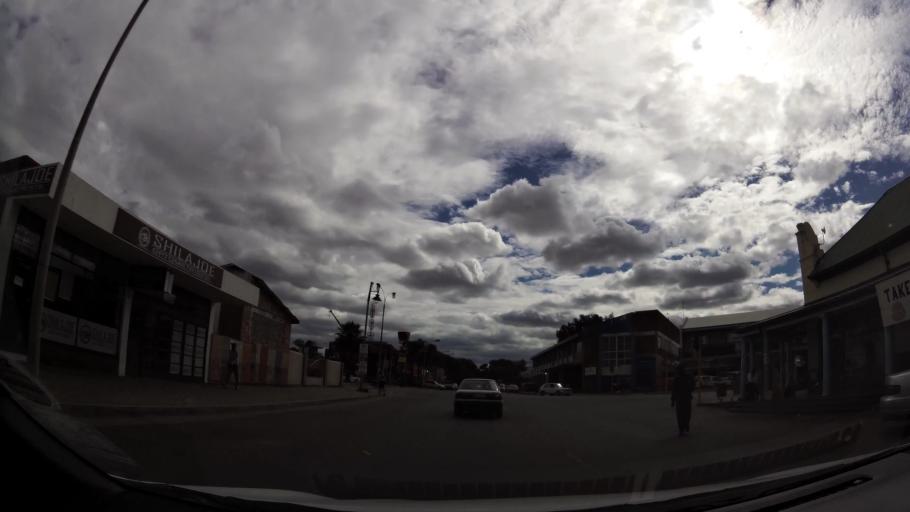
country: ZA
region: Limpopo
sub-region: Waterberg District Municipality
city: Bela-Bela
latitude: -24.8854
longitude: 28.2943
